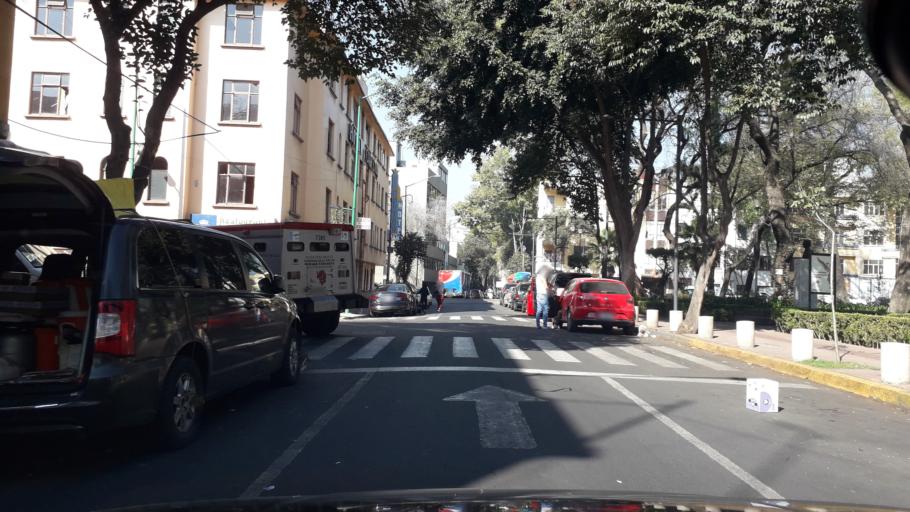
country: MX
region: Mexico City
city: Cuauhtemoc
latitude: 19.4374
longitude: -99.1519
